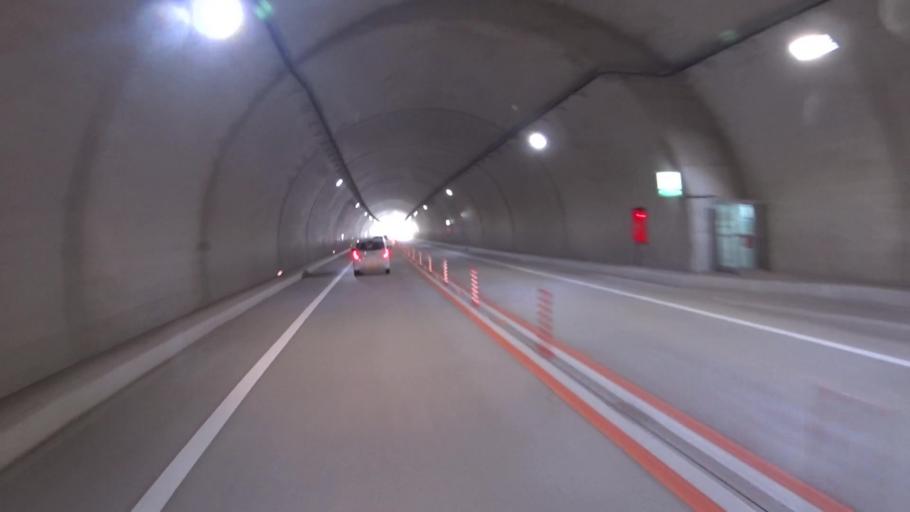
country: JP
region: Kyoto
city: Ayabe
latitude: 35.2074
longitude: 135.3475
